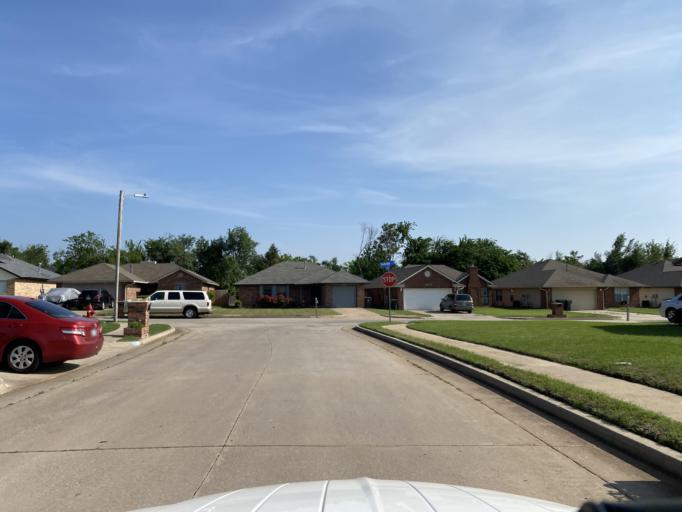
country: US
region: Oklahoma
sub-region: Oklahoma County
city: Spencer
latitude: 35.4902
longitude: -97.3755
